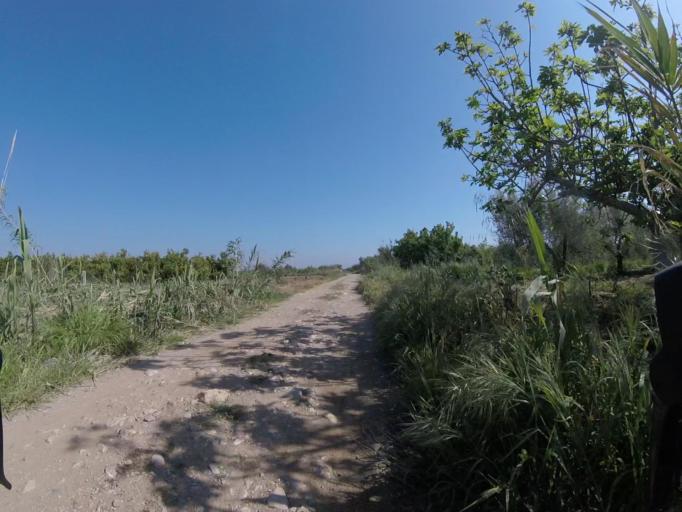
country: ES
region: Valencia
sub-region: Provincia de Castello
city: Orpesa/Oropesa del Mar
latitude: 40.1549
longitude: 0.1706
